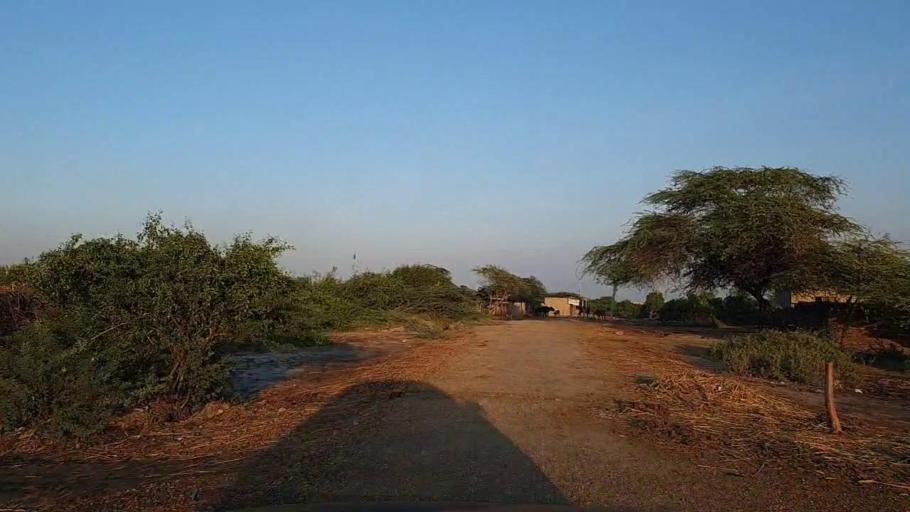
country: PK
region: Sindh
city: Thatta
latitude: 24.6646
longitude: 67.9192
